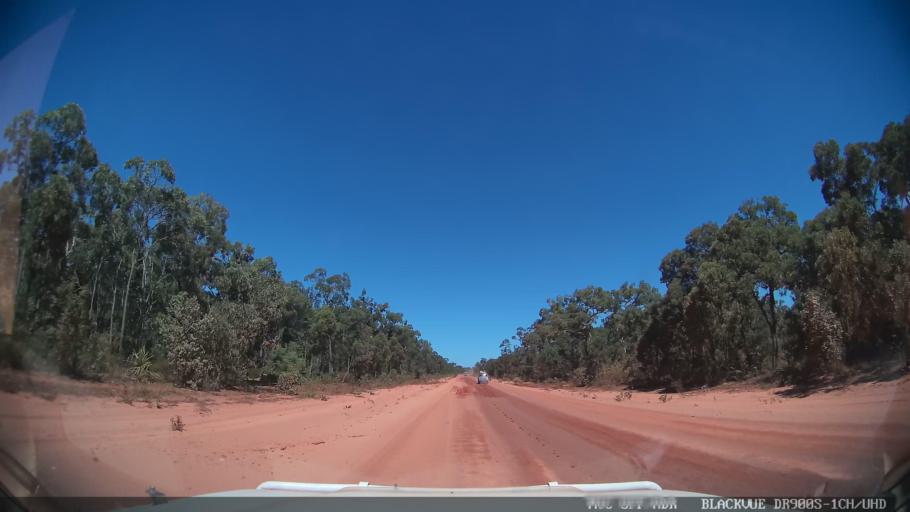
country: AU
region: Queensland
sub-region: Torres
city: Thursday Island
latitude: -11.3697
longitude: 142.3484
